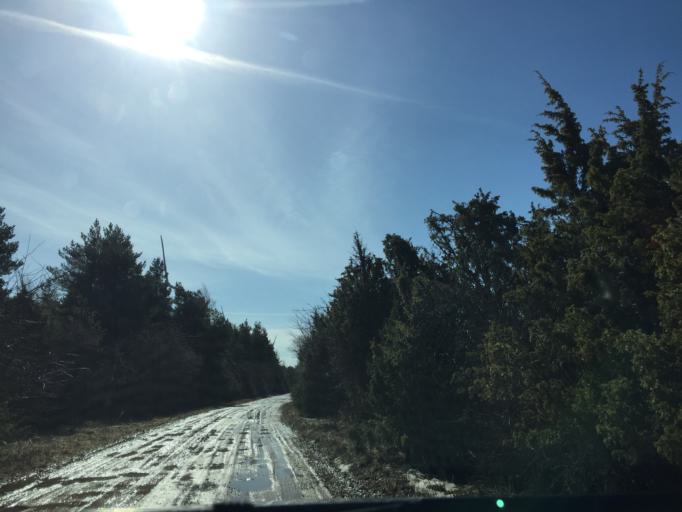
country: EE
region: Laeaene
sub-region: Haapsalu linn
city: Haapsalu
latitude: 58.6441
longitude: 23.5150
